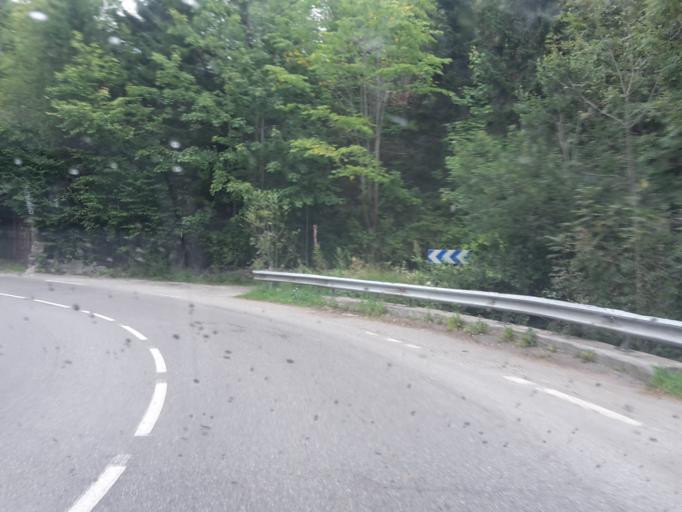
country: FR
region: Rhone-Alpes
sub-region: Departement de la Haute-Savoie
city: Domancy
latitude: 45.8909
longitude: 6.6695
